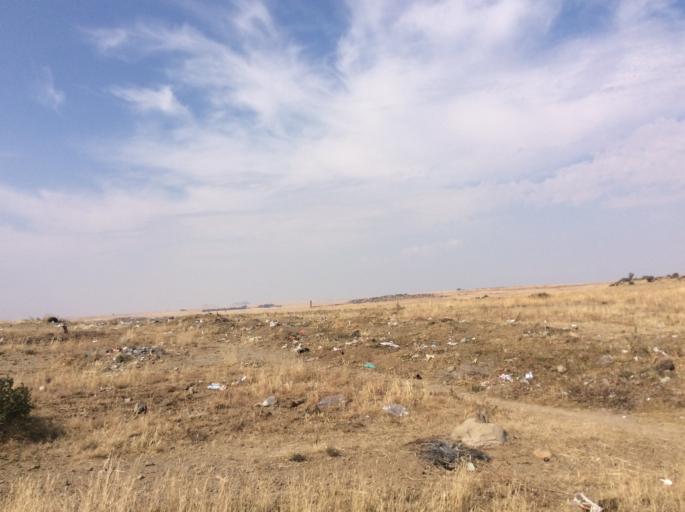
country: ZA
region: Orange Free State
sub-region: Xhariep District Municipality
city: Dewetsdorp
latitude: -29.5940
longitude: 26.6850
